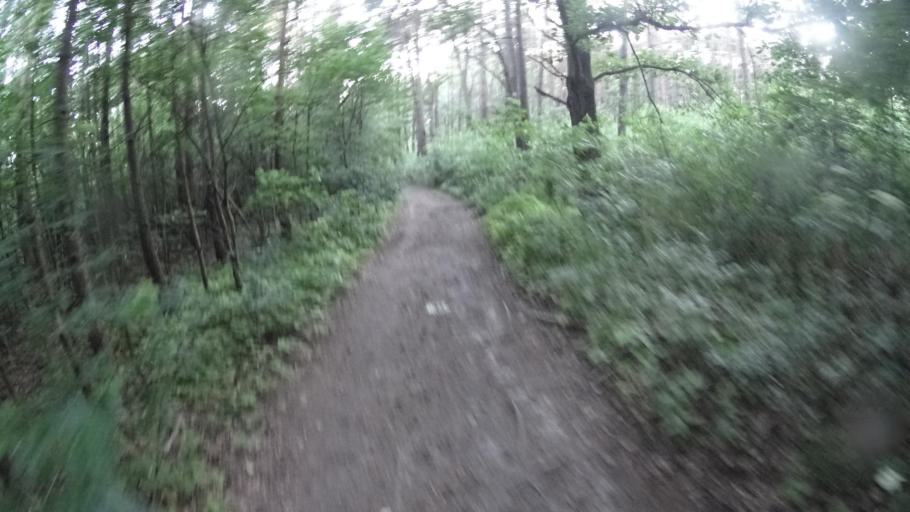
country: PL
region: Masovian Voivodeship
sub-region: Powiat warszawski zachodni
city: Truskaw
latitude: 52.2765
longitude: 20.7757
